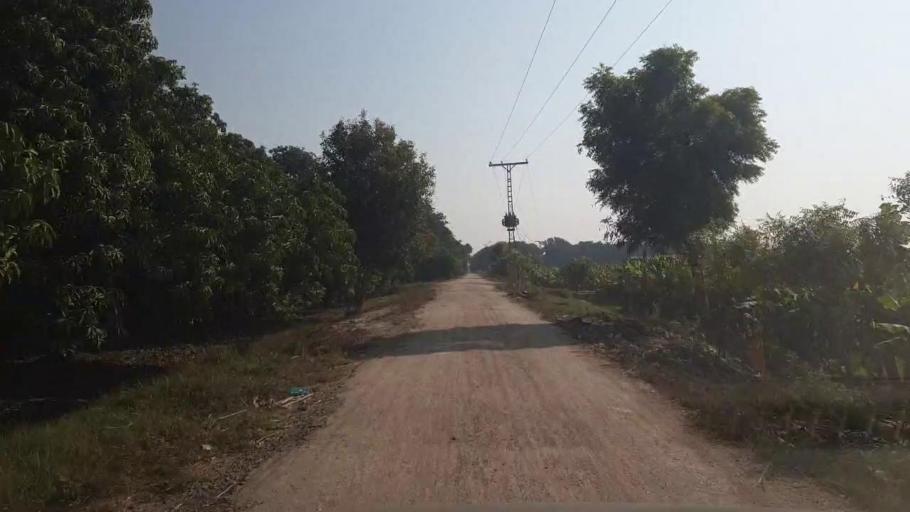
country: PK
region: Sindh
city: Tando Allahyar
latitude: 25.4642
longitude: 68.7788
